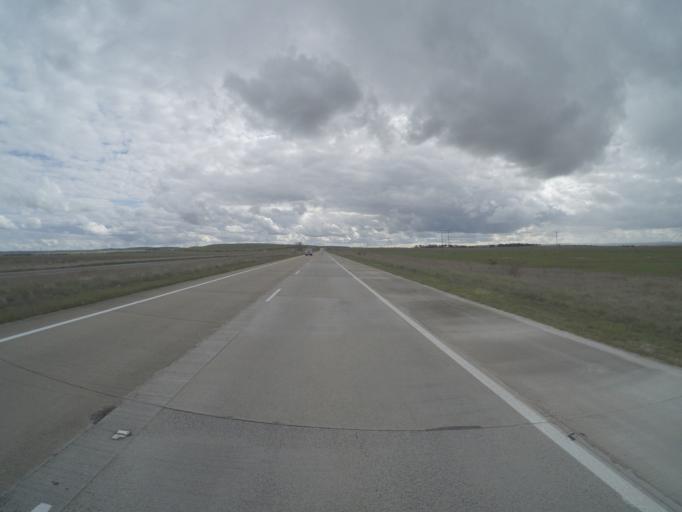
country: AU
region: New South Wales
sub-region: Goulburn Mulwaree
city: Goulburn
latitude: -34.8071
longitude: 149.5551
